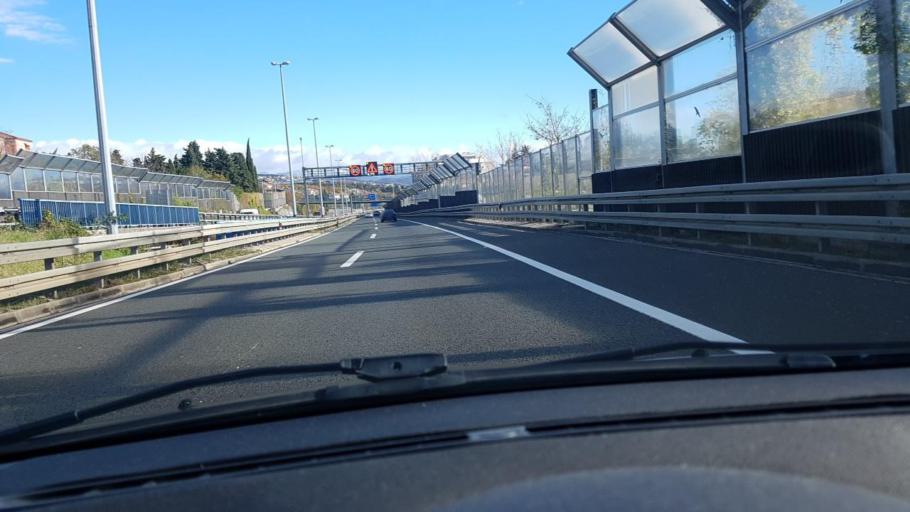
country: HR
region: Primorsko-Goranska
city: Marinici
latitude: 45.3454
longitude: 14.3803
